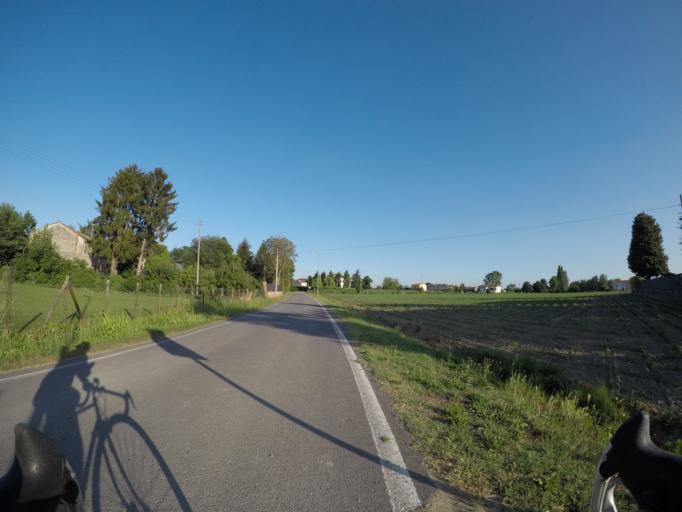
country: IT
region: Veneto
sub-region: Provincia di Rovigo
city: Villamarzana
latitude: 45.0250
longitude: 11.6759
